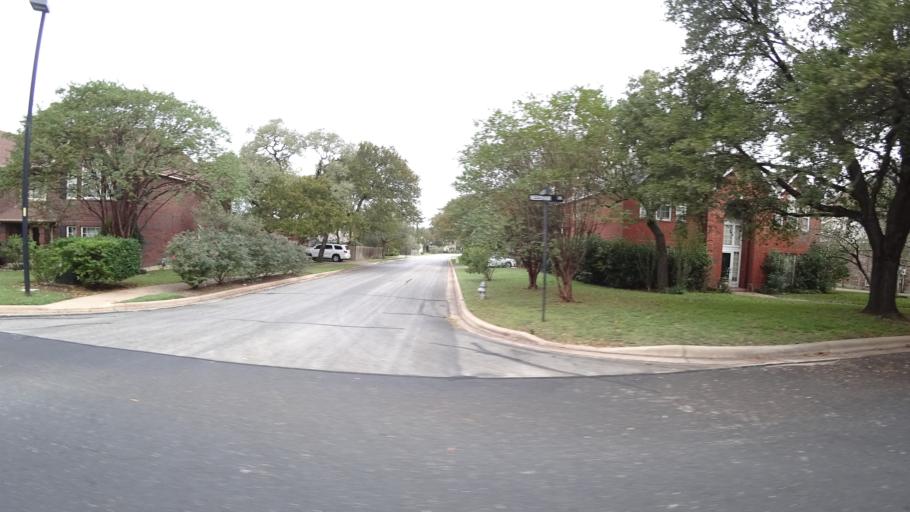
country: US
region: Texas
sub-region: Travis County
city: Shady Hollow
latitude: 30.1926
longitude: -97.8931
